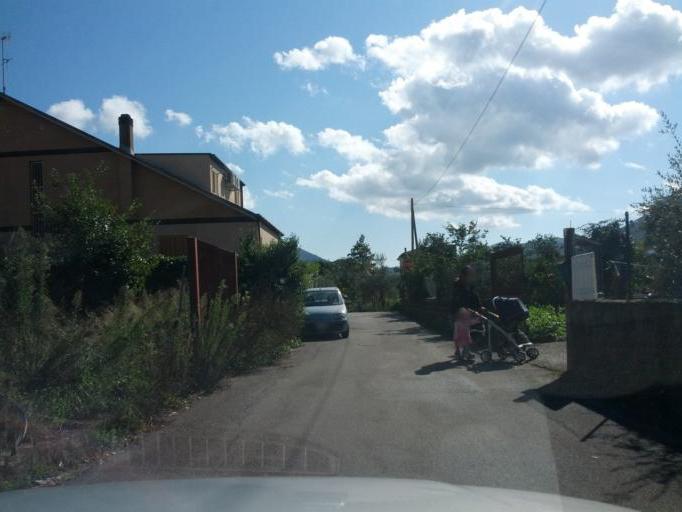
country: IT
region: Latium
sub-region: Provincia di Latina
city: Fondi
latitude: 41.3459
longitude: 13.4435
